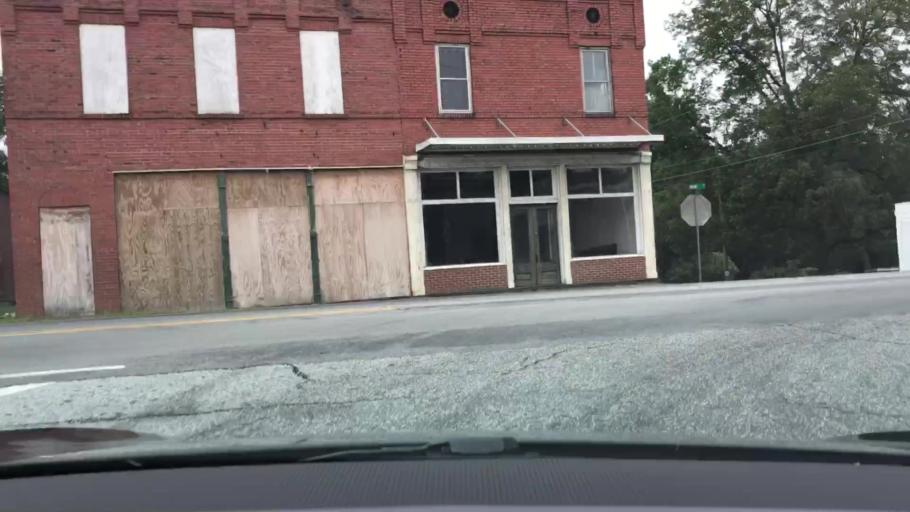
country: US
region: Georgia
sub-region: Greene County
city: Union Point
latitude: 33.5366
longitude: -83.0812
